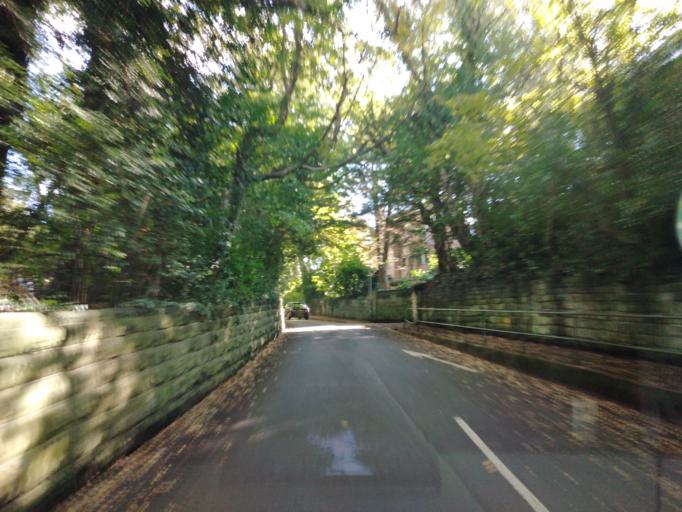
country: GB
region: England
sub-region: East Sussex
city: Saint Leonards-on-Sea
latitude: 50.8640
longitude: 0.5471
